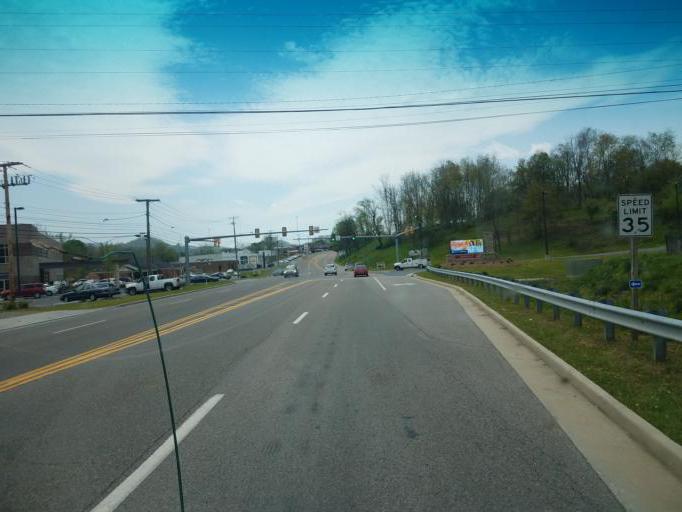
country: US
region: Virginia
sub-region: Smyth County
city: Marion
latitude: 36.8492
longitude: -81.4890
